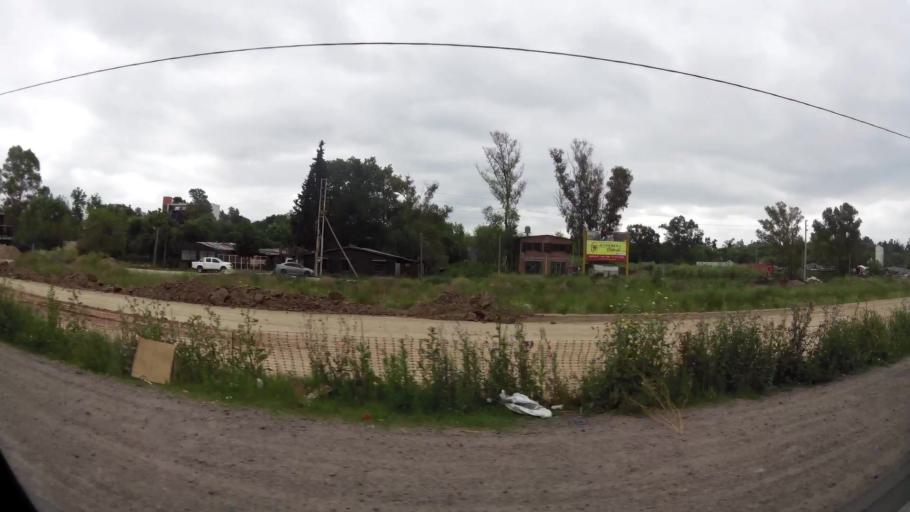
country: AR
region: Buenos Aires
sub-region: Partido de Ezeiza
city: Ezeiza
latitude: -34.8932
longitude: -58.5073
